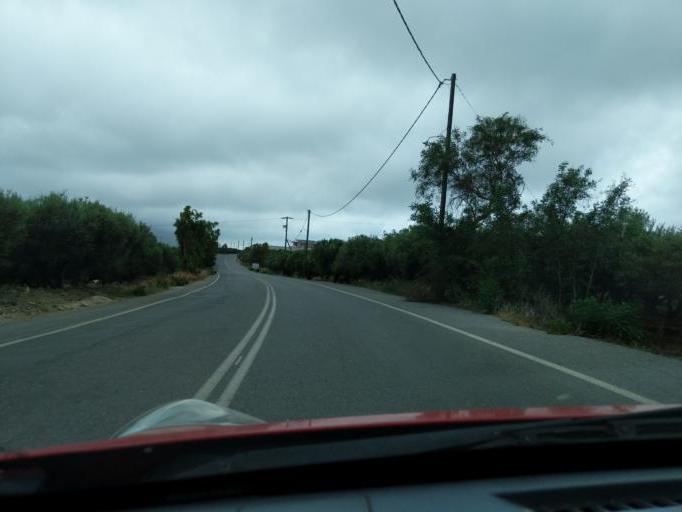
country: GR
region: Crete
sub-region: Nomos Chanias
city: Platanos
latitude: 35.4770
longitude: 23.6044
